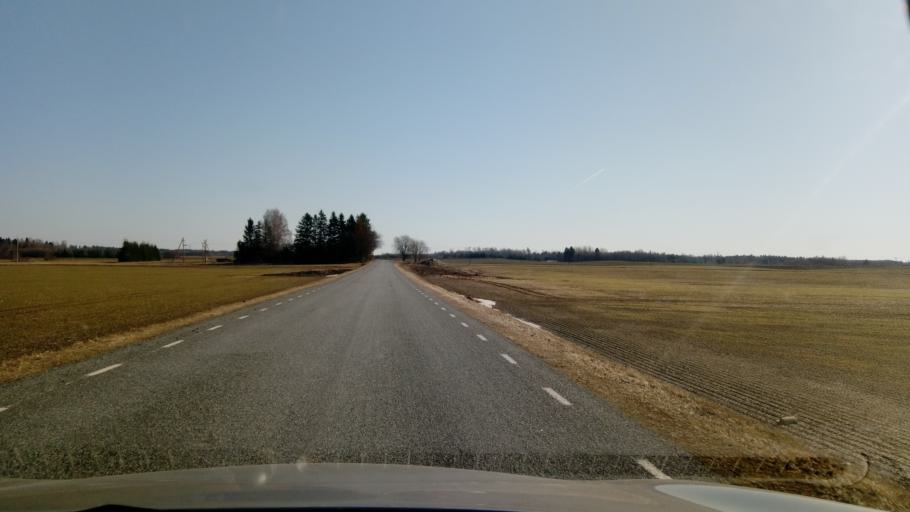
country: EE
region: Laeaene-Virumaa
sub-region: Kadrina vald
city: Kadrina
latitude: 59.2596
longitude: 26.2409
